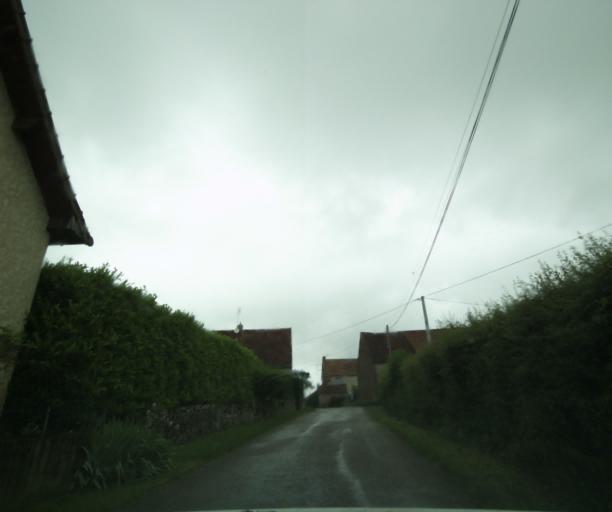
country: FR
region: Bourgogne
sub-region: Departement de Saone-et-Loire
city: Charolles
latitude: 46.4283
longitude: 4.3515
